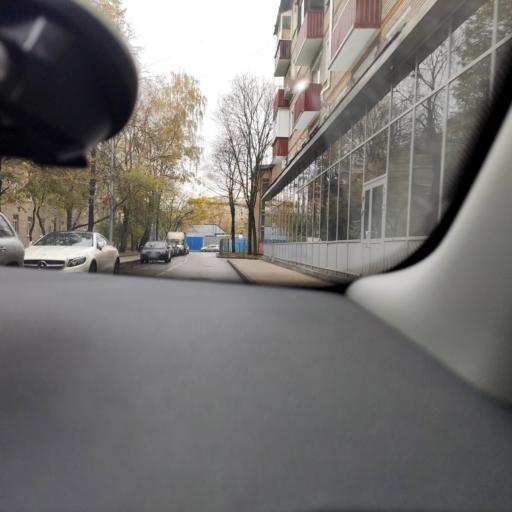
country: RU
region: Moskovskaya
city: Koptevo
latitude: 55.8137
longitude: 37.4918
